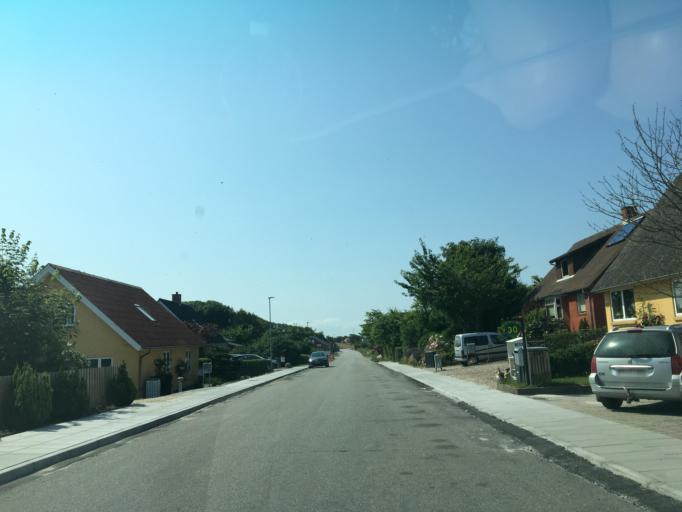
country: DK
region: North Denmark
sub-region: Thisted Kommune
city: Hurup
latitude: 56.8181
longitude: 8.4862
